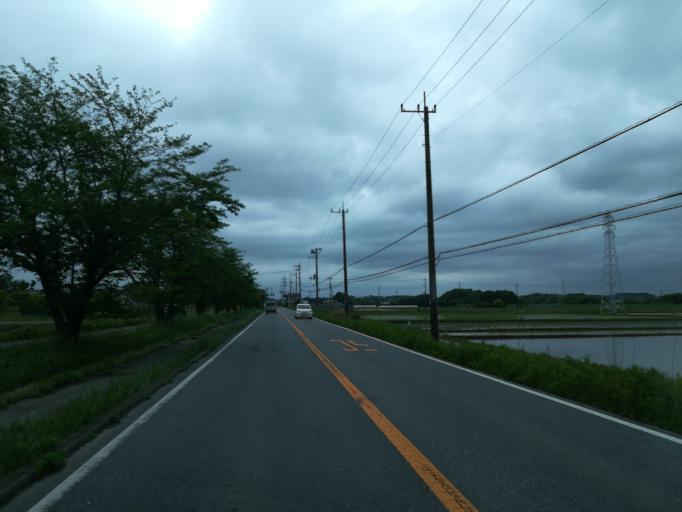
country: JP
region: Ibaraki
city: Tsukuba
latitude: 36.1855
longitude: 140.0790
